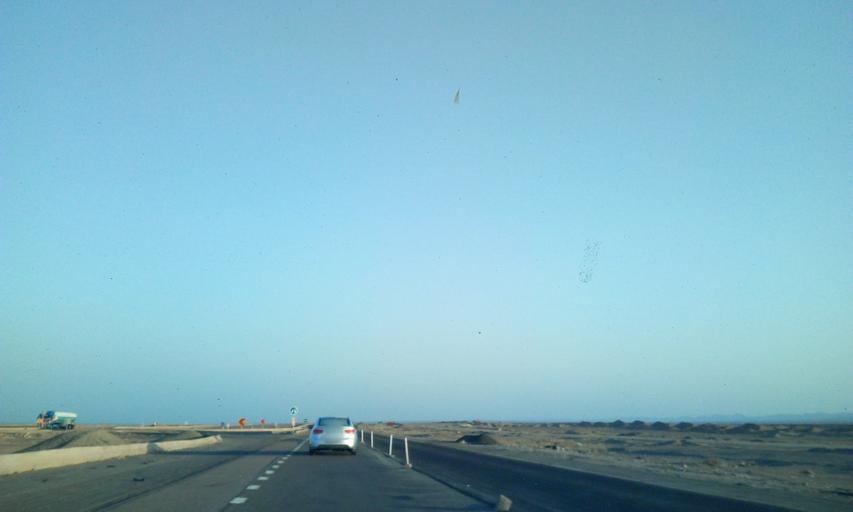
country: EG
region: South Sinai
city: Tor
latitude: 27.8895
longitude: 33.4089
